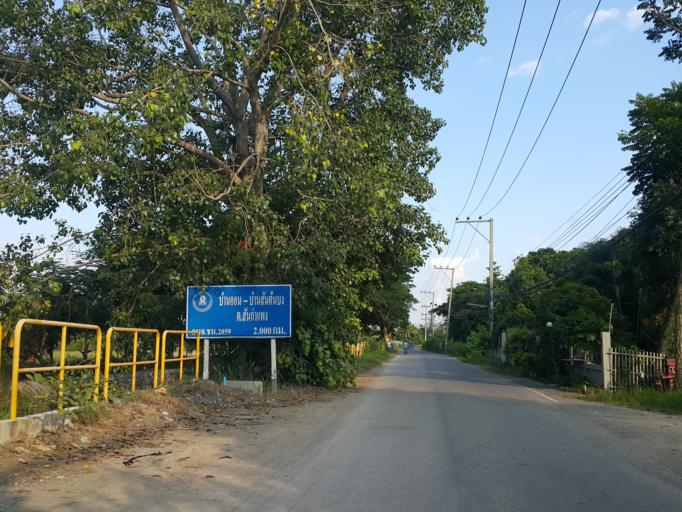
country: TH
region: Chiang Mai
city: San Kamphaeng
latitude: 18.7453
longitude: 99.0979
